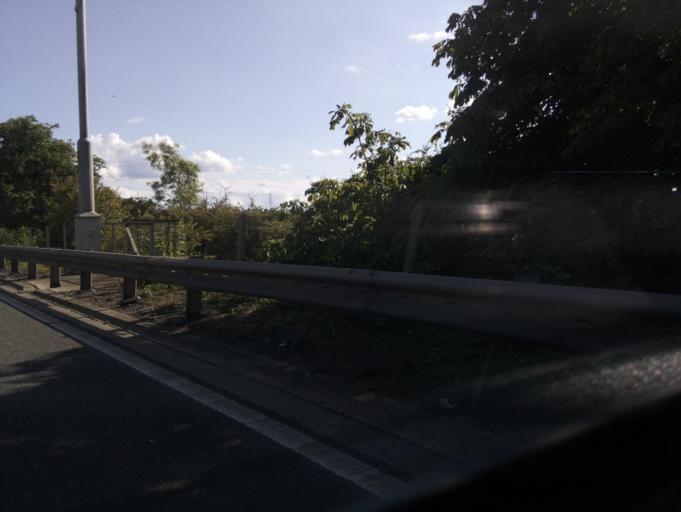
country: GB
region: England
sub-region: Central Bedfordshire
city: Chalton
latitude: 51.9327
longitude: -0.4971
